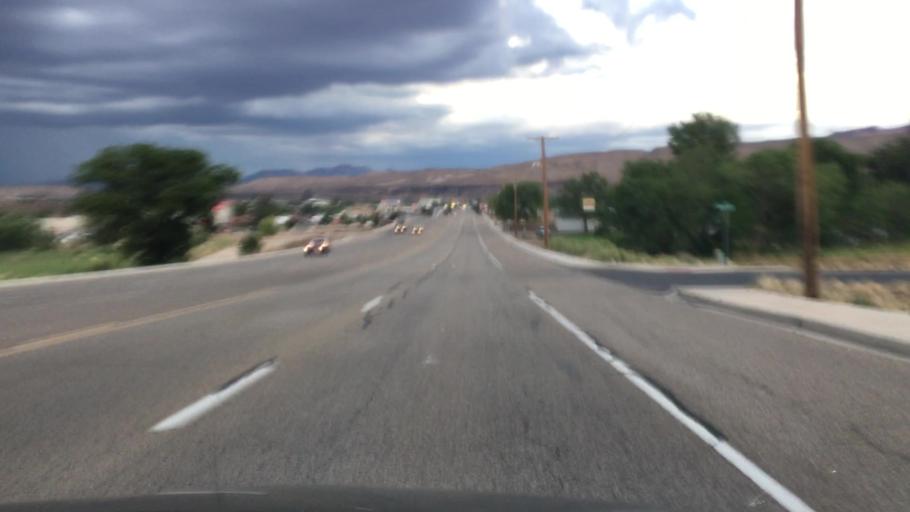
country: US
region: Utah
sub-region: Washington County
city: Hurricane
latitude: 37.1763
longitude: -113.3217
